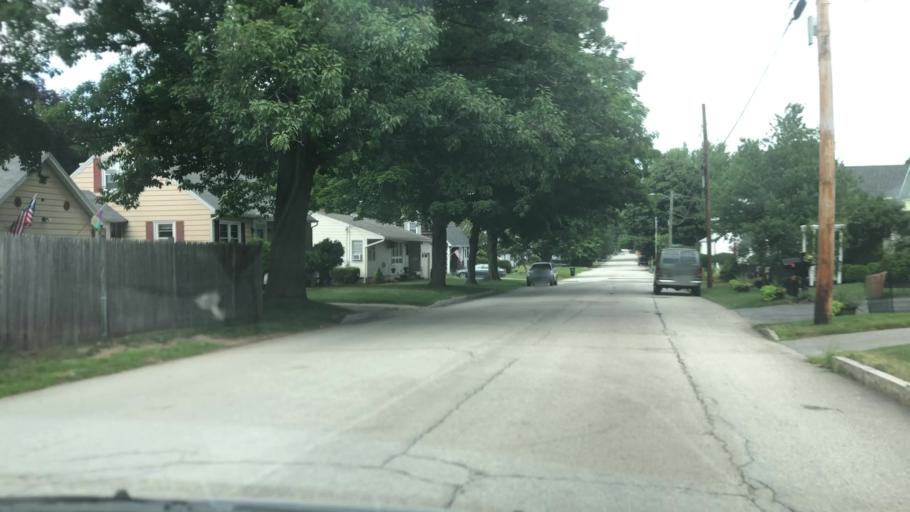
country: US
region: New Hampshire
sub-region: Hillsborough County
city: Manchester
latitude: 42.9766
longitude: -71.4333
